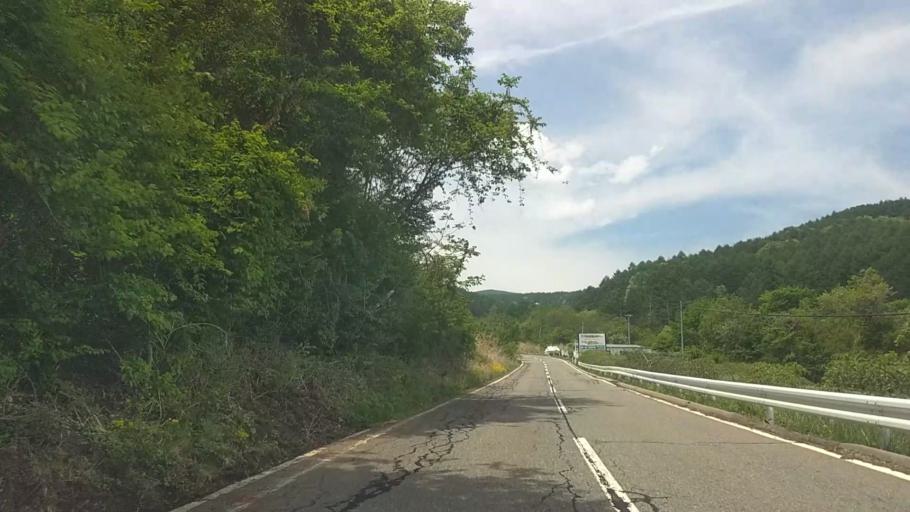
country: JP
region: Nagano
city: Saku
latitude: 36.1042
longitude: 138.4232
